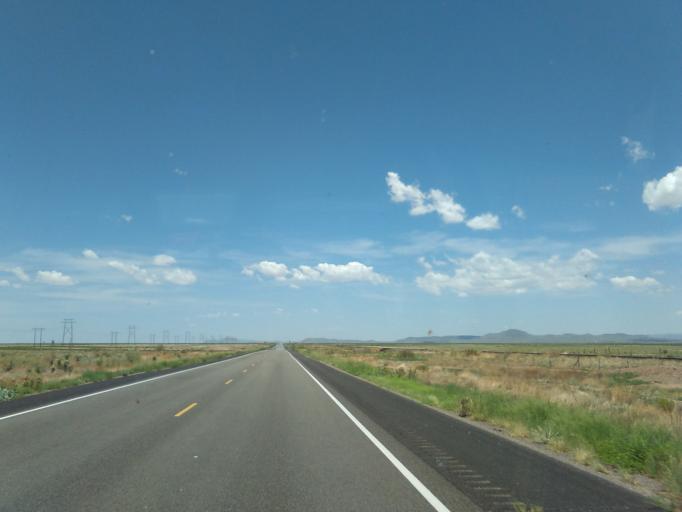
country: US
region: New Mexico
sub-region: Luna County
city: Deming
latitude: 32.3934
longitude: -107.5952
